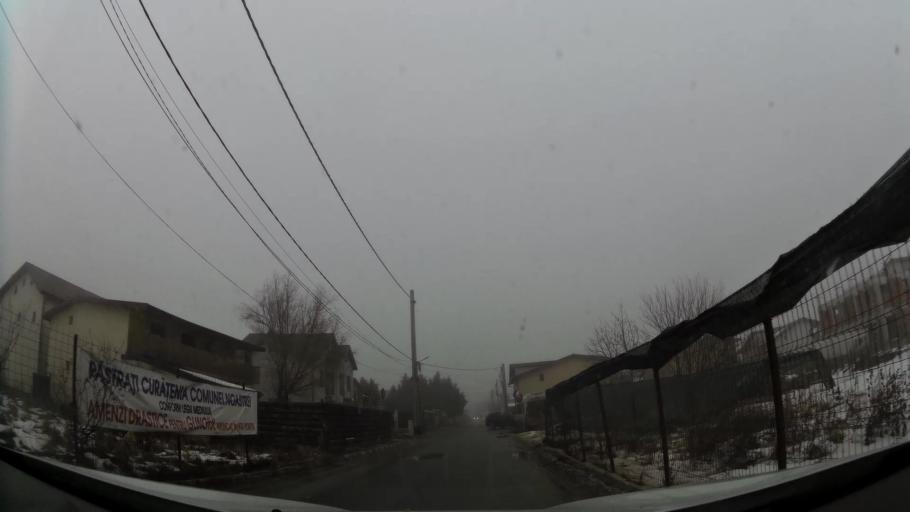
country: RO
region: Ilfov
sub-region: Comuna Chiajna
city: Chiajna
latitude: 44.4544
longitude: 25.9757
